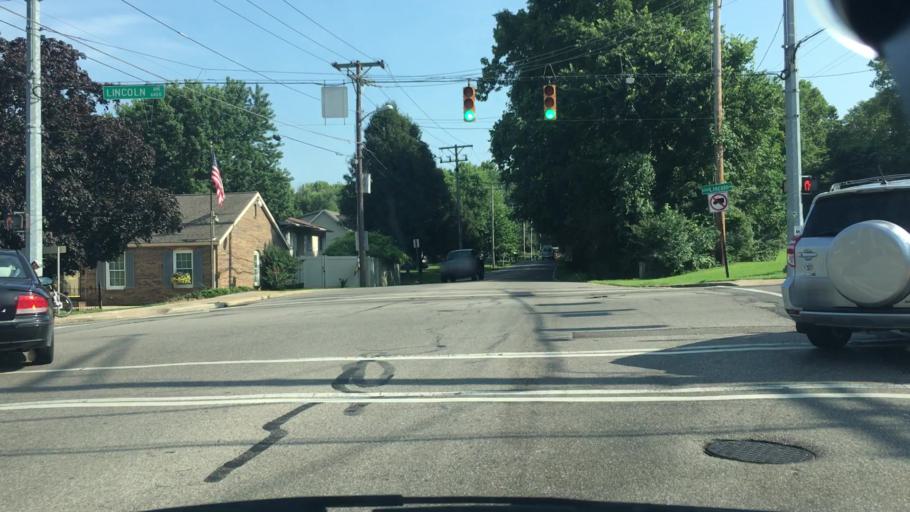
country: US
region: Indiana
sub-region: Vanderburgh County
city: Melody Hill
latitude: 37.9695
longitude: -87.4744
